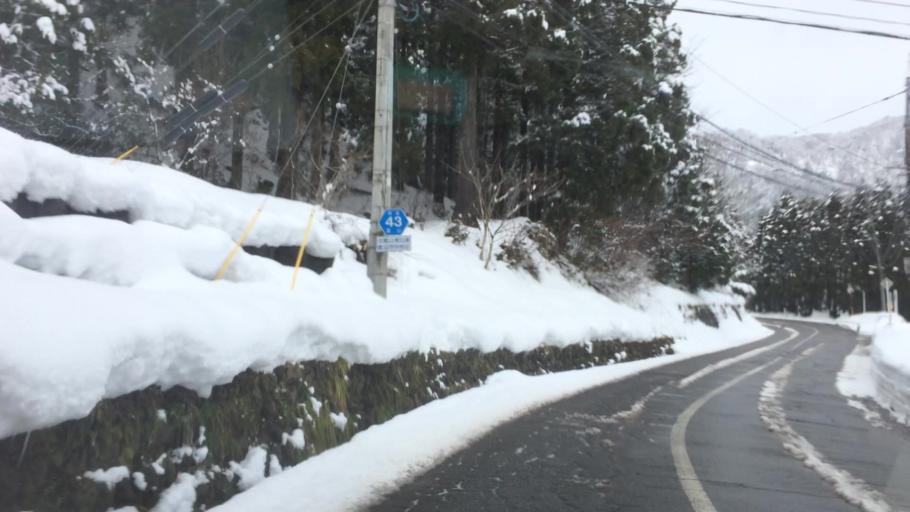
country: JP
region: Toyama
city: Kamiichi
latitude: 36.5678
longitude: 137.3638
